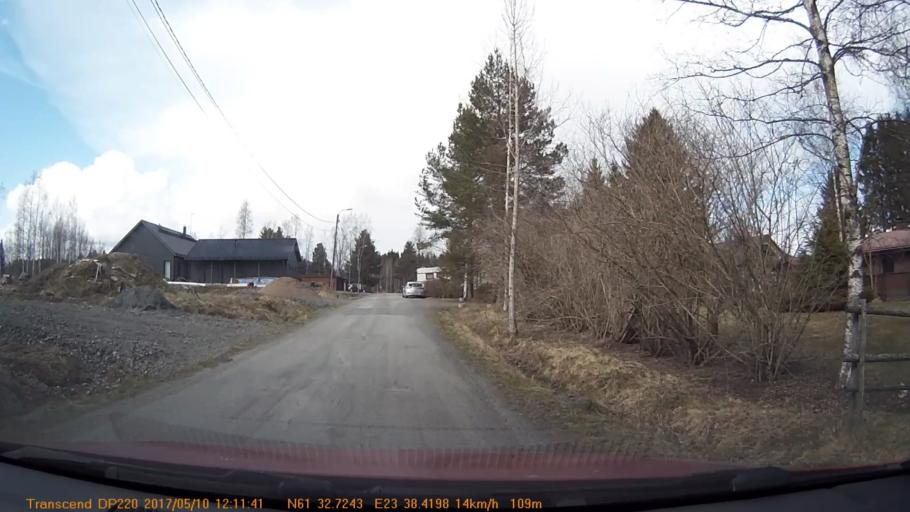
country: FI
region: Pirkanmaa
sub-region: Tampere
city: Yloejaervi
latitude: 61.5454
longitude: 23.6403
